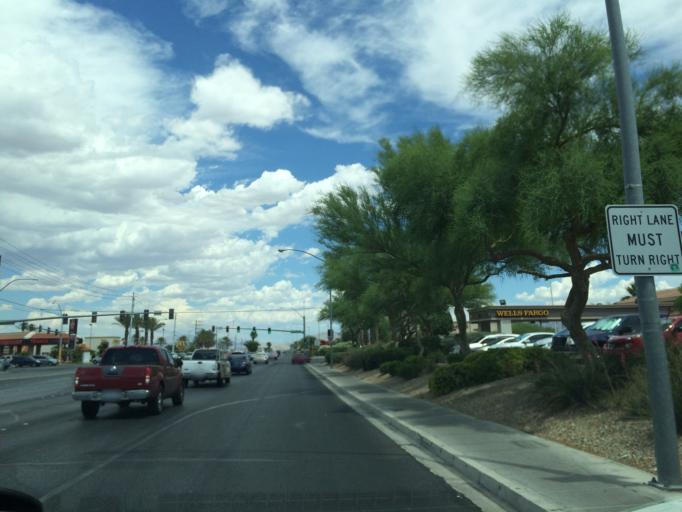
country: US
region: Nevada
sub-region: Clark County
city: North Las Vegas
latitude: 36.2393
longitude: -115.1632
